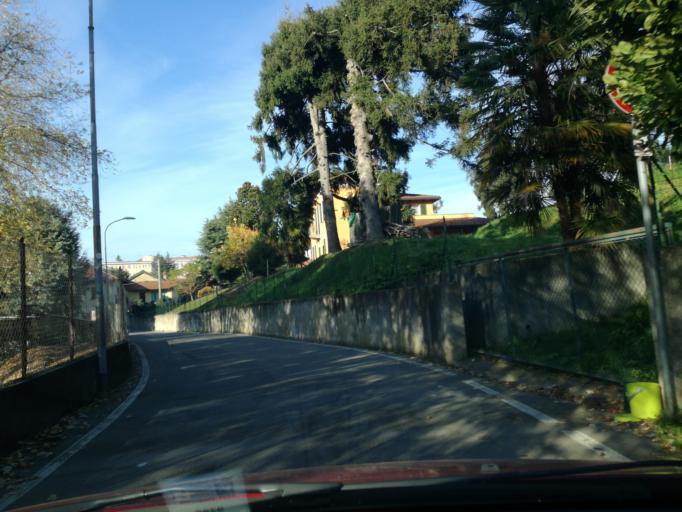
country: IT
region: Lombardy
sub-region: Provincia di Lecco
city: Robbiate
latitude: 45.6967
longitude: 9.4309
